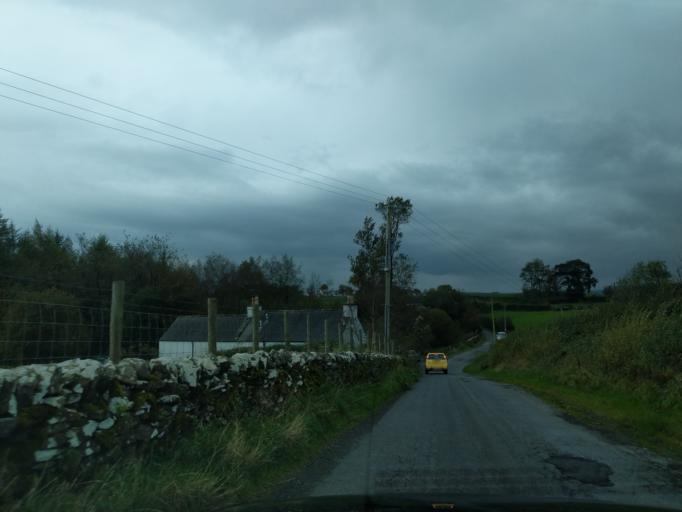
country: GB
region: Scotland
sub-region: Dumfries and Galloway
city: Castle Douglas
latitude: 54.9210
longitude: -3.9567
